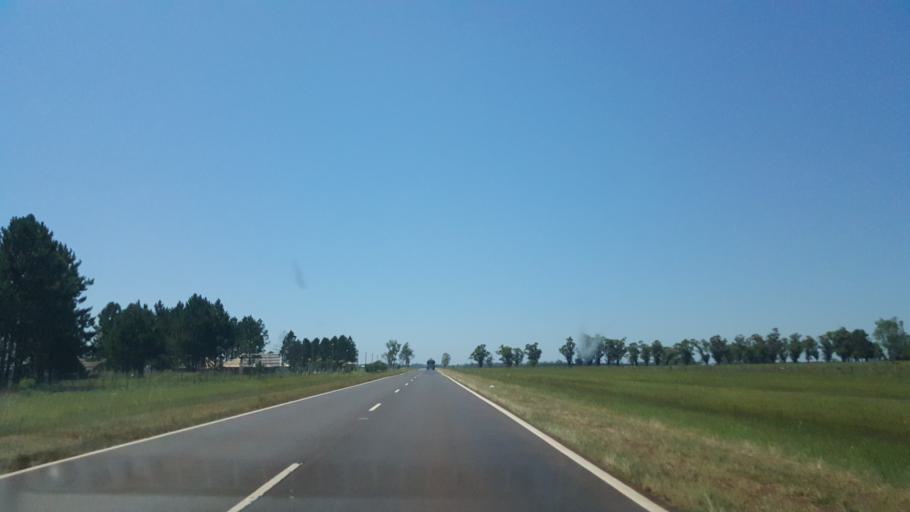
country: AR
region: Corrientes
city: Santo Tome
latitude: -28.5182
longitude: -56.1064
